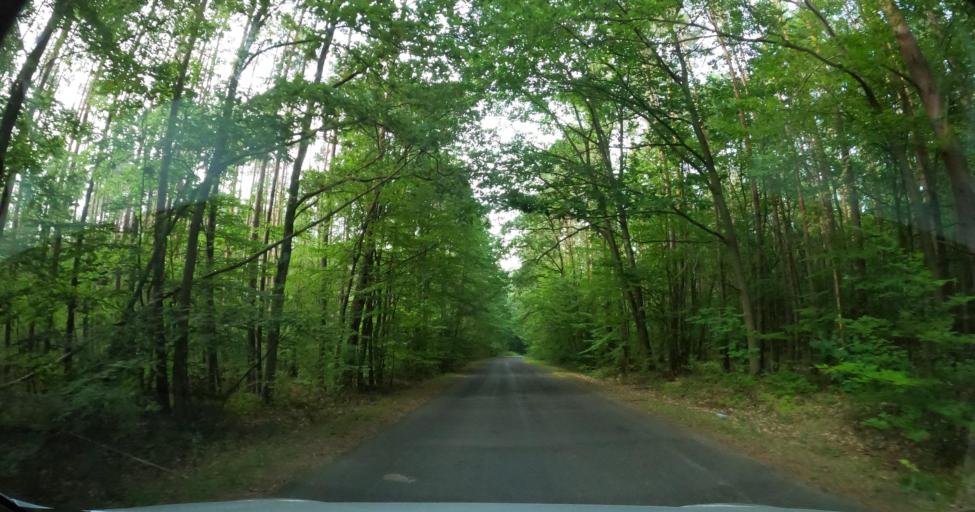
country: PL
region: West Pomeranian Voivodeship
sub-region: Powiat goleniowski
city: Goleniow
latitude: 53.5178
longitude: 14.8566
